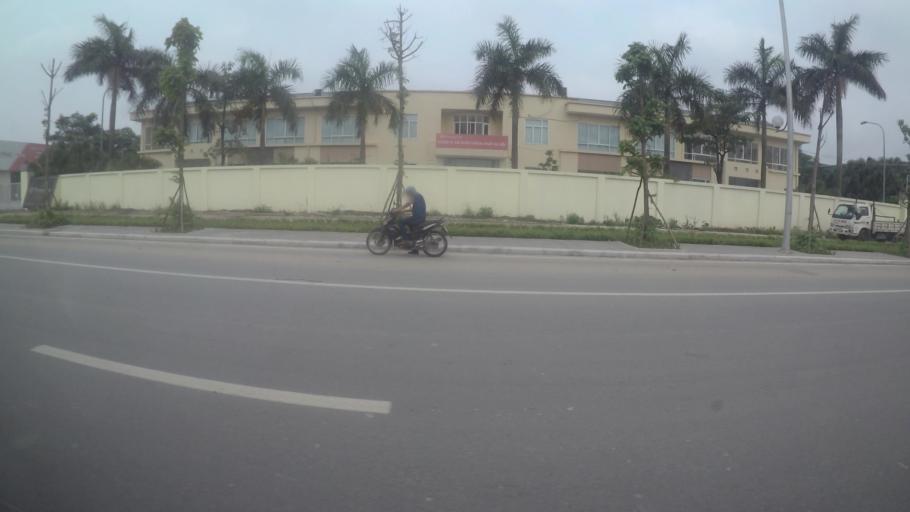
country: VN
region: Ha Noi
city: Cau Dien
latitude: 21.0451
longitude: 105.7368
